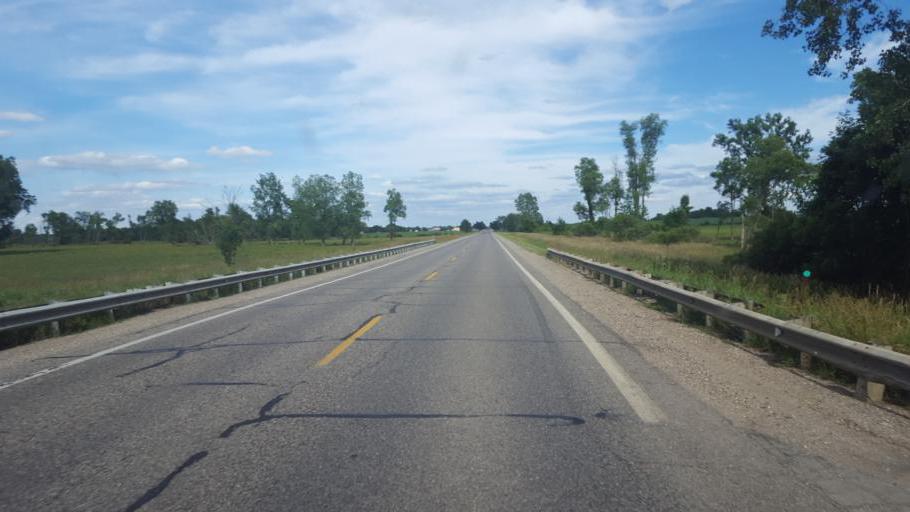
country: US
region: Michigan
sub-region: Eaton County
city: Charlotte
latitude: 42.5680
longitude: -84.9348
